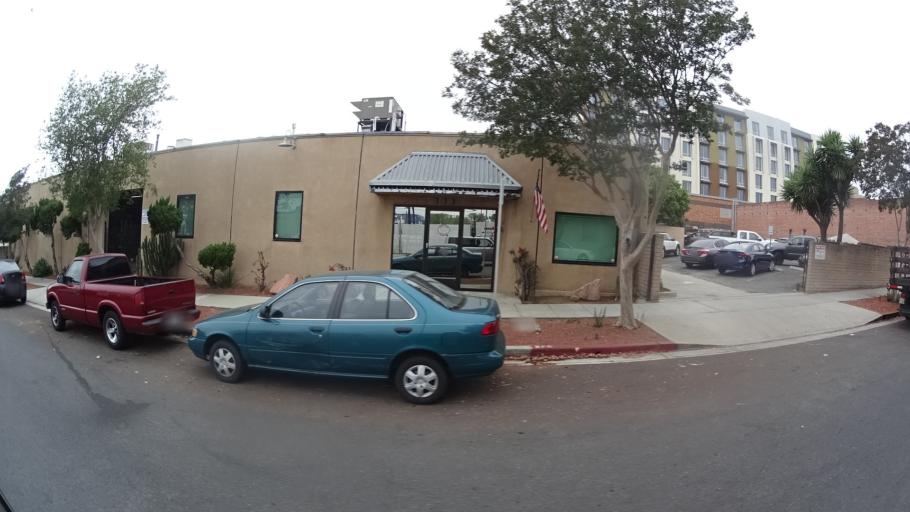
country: US
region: California
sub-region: Los Angeles County
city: Burbank
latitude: 34.1773
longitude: -118.3055
